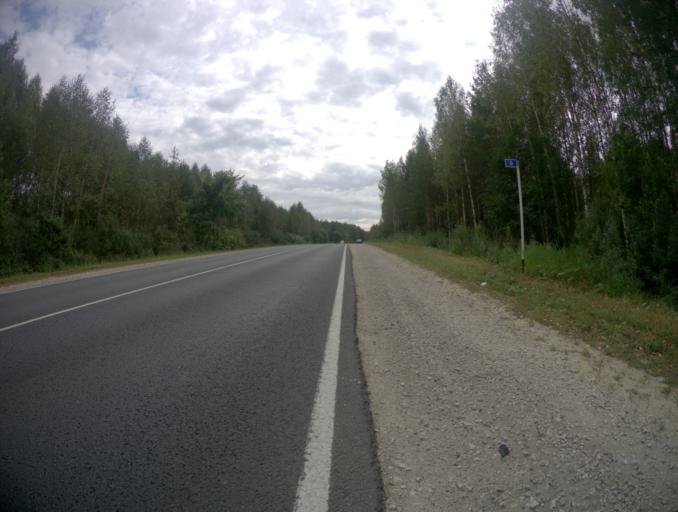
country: RU
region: Vladimir
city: Golovino
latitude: 55.9488
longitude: 40.5783
